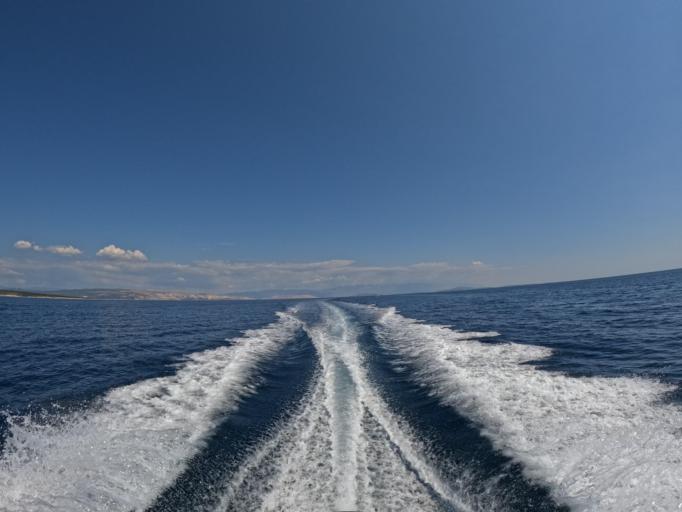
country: HR
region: Primorsko-Goranska
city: Cres
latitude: 44.9377
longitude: 14.5007
